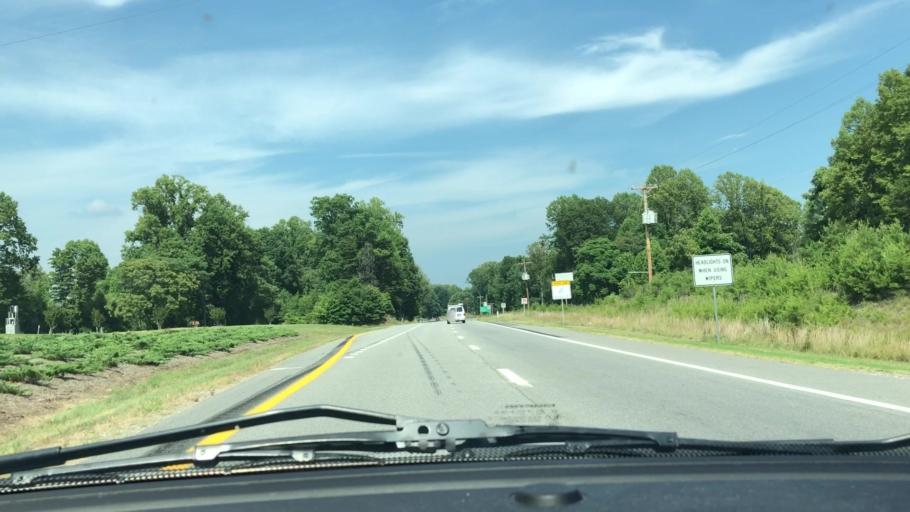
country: US
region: North Carolina
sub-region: Rockingham County
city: Stoneville
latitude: 36.5451
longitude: -79.9066
